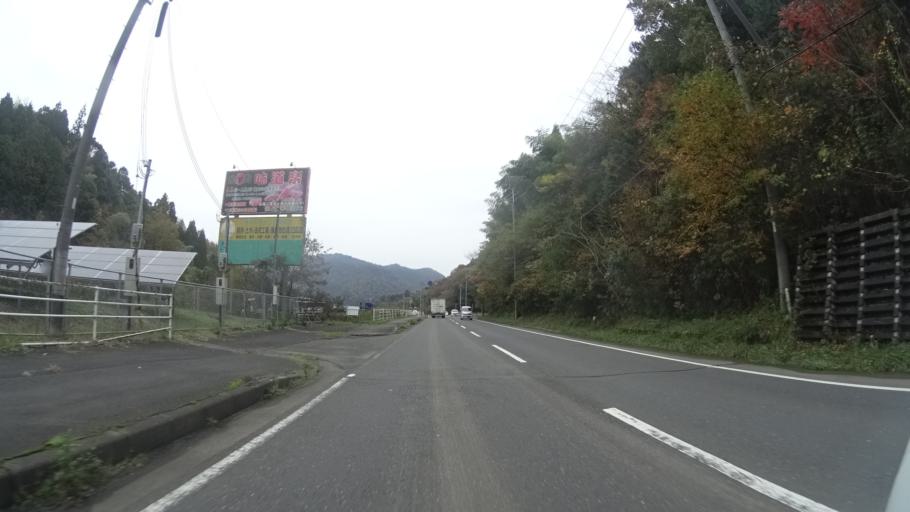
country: JP
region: Kyoto
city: Maizuru
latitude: 35.4713
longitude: 135.4244
